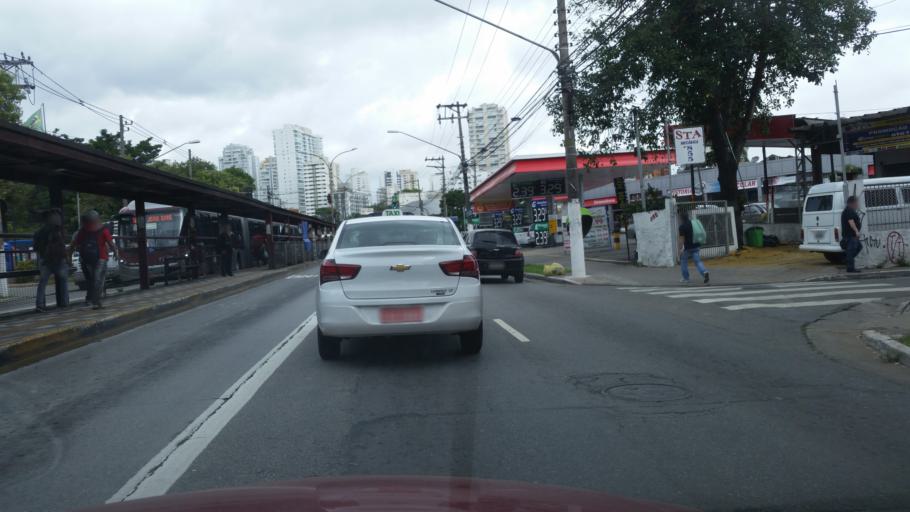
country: BR
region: Sao Paulo
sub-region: Taboao Da Serra
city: Taboao da Serra
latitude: -23.6461
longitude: -46.7096
